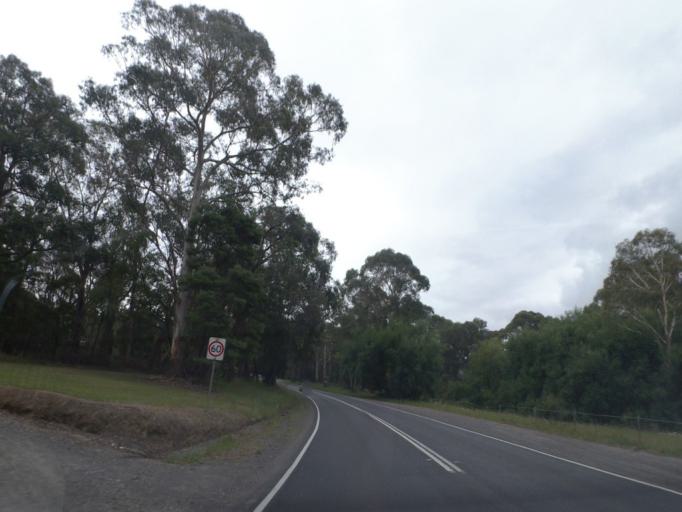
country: AU
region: Victoria
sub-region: Yarra Ranges
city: Mount Evelyn
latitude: -37.7956
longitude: 145.3760
